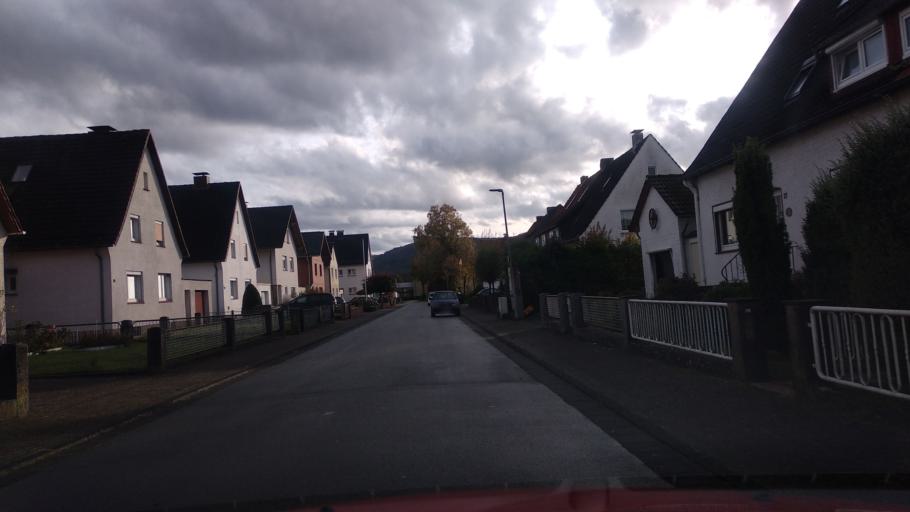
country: DE
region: North Rhine-Westphalia
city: Beverungen
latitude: 51.6717
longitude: 9.3735
